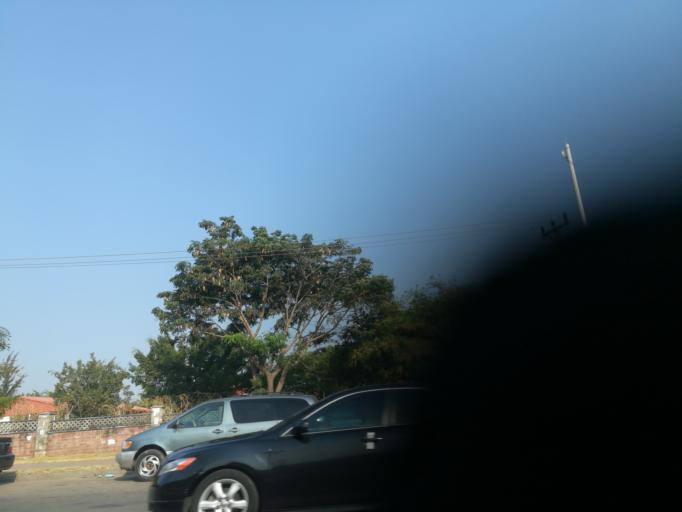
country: NG
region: Abuja Federal Capital Territory
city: Abuja
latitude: 9.0666
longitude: 7.4467
